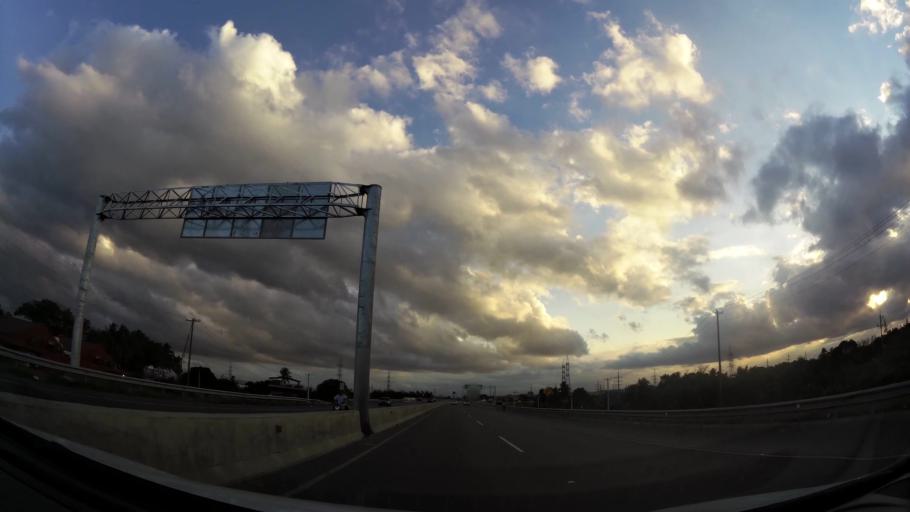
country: DO
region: Santiago
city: Licey al Medio
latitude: 19.4178
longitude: -70.6408
